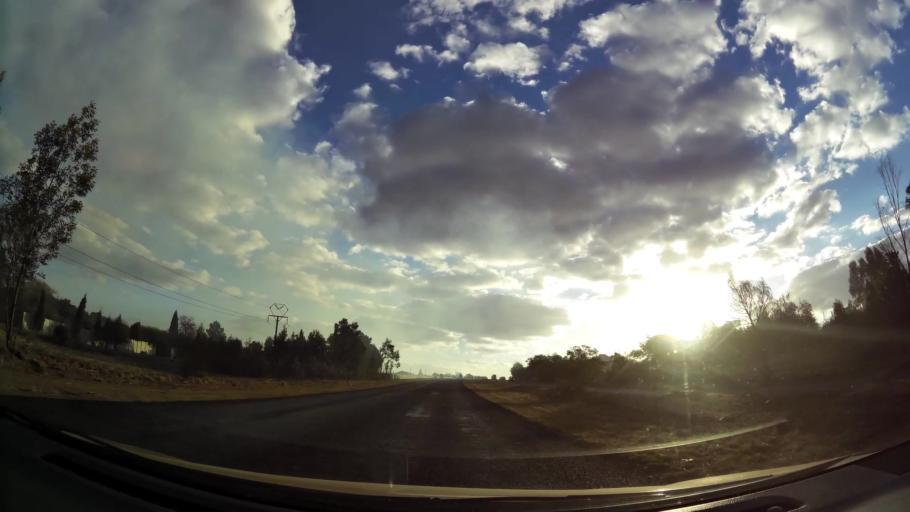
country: ZA
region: Gauteng
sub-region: City of Johannesburg Metropolitan Municipality
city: Midrand
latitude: -25.9479
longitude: 28.1613
